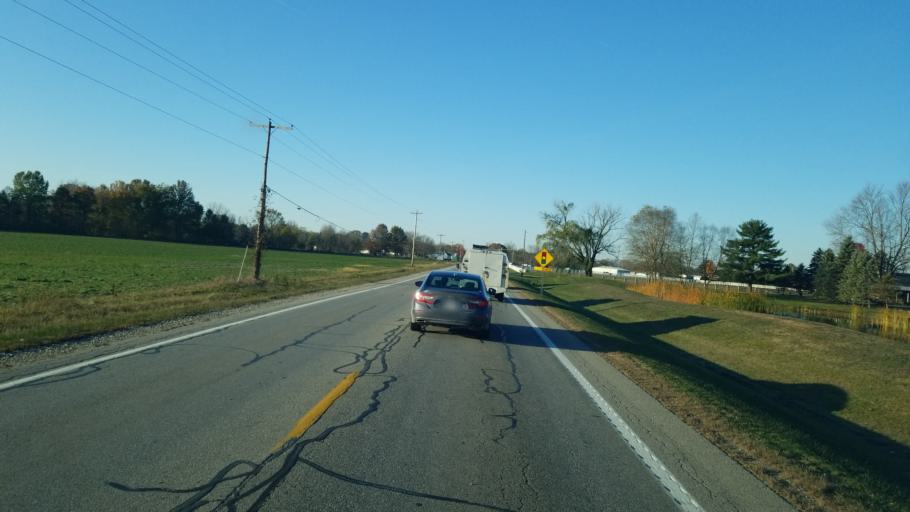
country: US
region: Ohio
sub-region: Delaware County
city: Delaware
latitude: 40.2601
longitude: -83.1249
